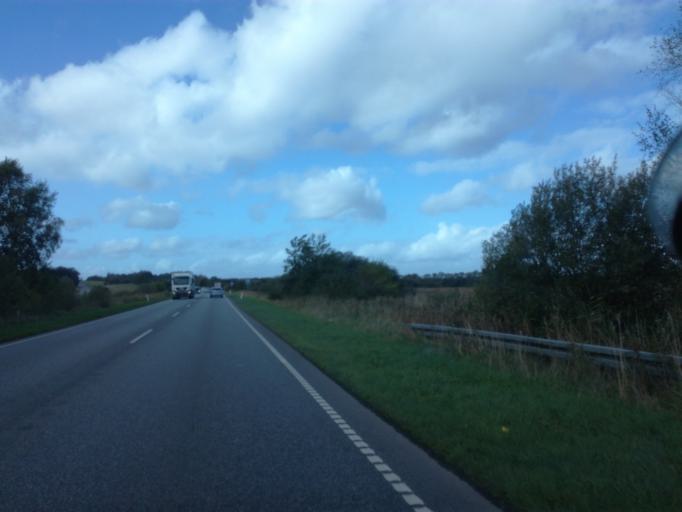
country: DK
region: South Denmark
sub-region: Fredericia Kommune
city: Fredericia
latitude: 55.6218
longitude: 9.7397
